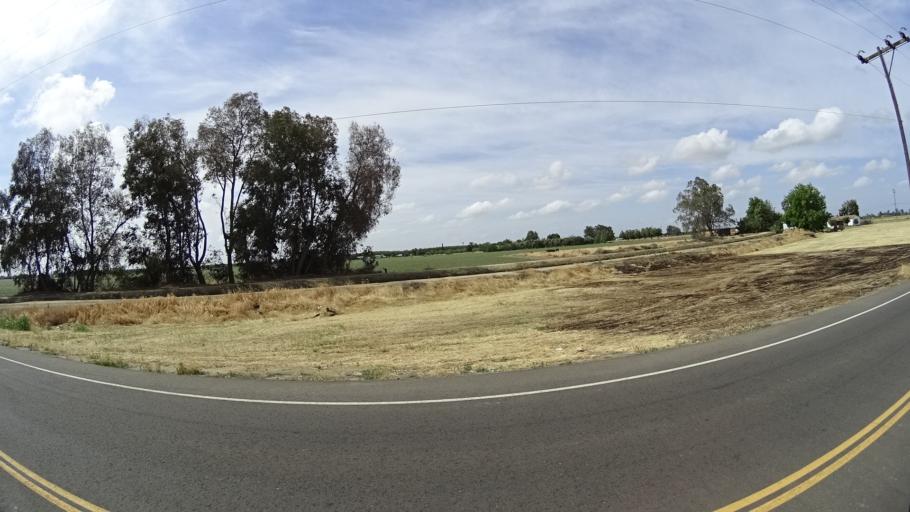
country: US
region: California
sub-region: Kings County
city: Hanford
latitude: 36.3057
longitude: -119.6709
